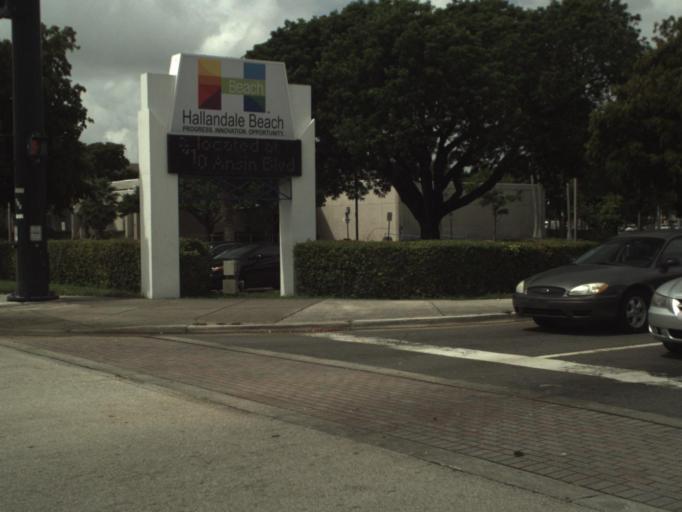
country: US
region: Florida
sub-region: Broward County
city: Hallandale Beach
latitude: 25.9820
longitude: -80.1423
